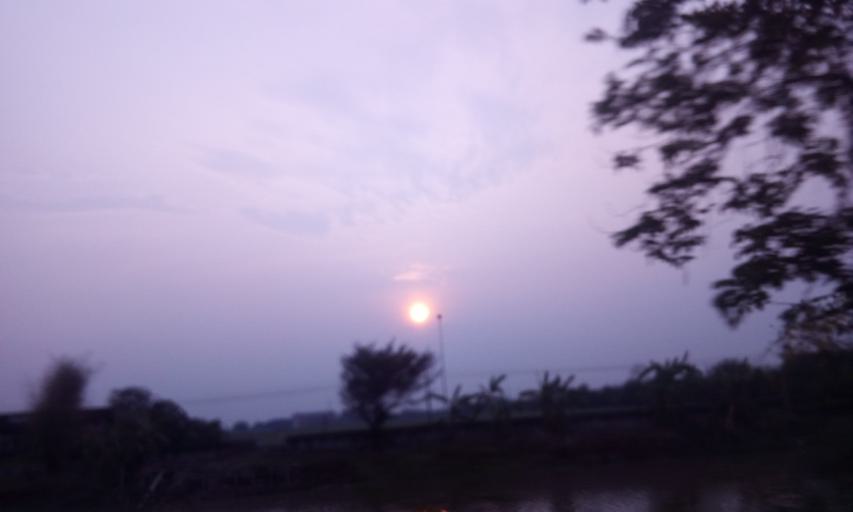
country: TH
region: Bangkok
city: Nong Chok
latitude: 13.9459
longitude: 100.8949
